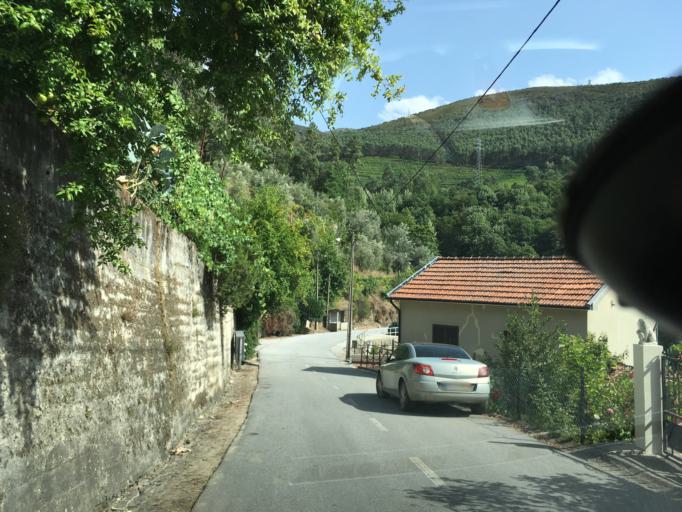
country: PT
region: Braga
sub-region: Celorico de Basto
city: Celorico de Basto
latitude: 41.3215
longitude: -7.9712
